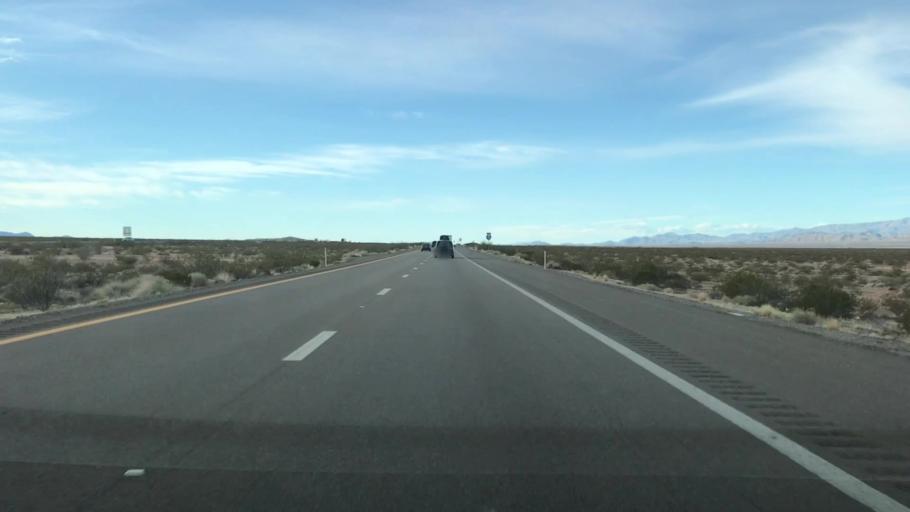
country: US
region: Nevada
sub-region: Clark County
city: Moapa Town
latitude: 36.6337
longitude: -114.6040
